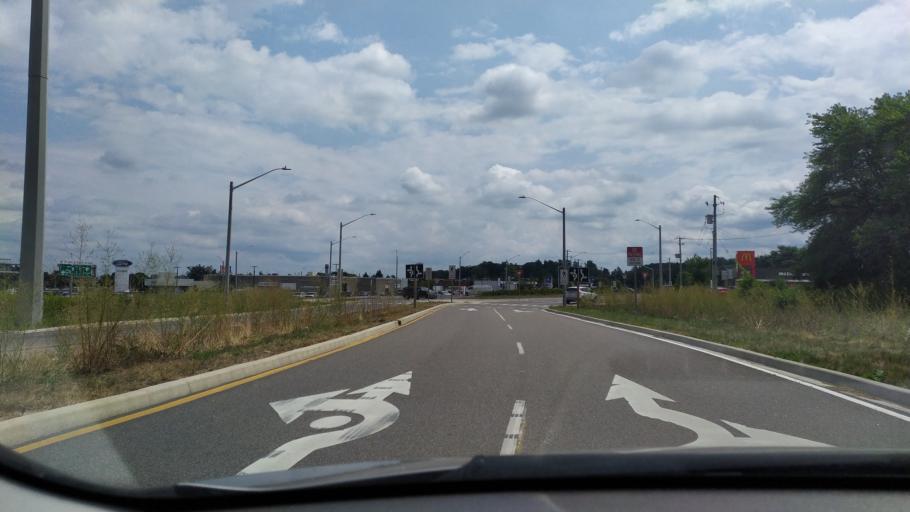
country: CA
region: Ontario
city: Kitchener
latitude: 43.4260
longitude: -80.4847
